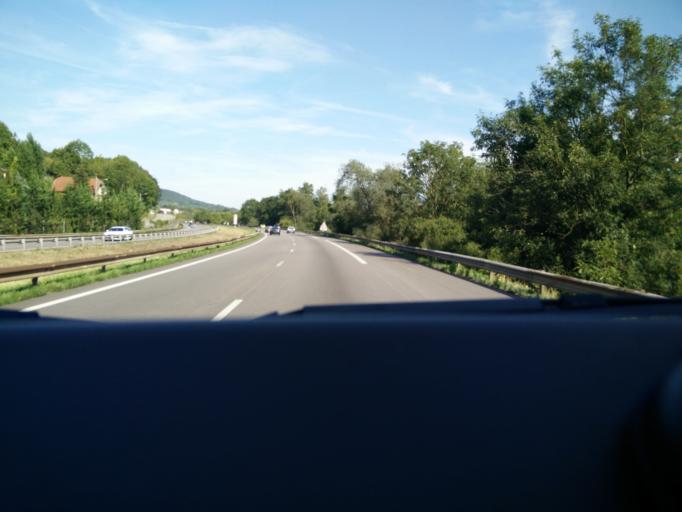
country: FR
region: Lorraine
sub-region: Departement de Meurthe-et-Moselle
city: Custines
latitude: 48.7910
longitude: 6.1252
